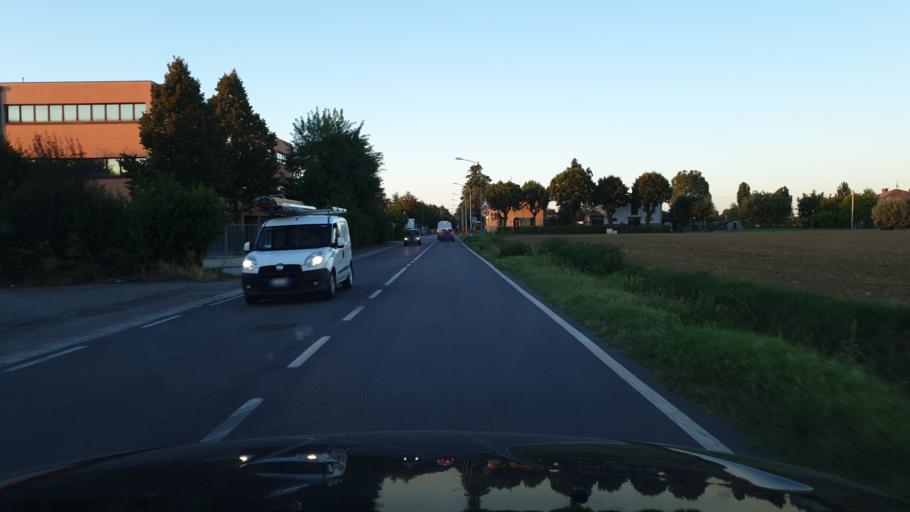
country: IT
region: Emilia-Romagna
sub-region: Provincia di Bologna
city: Quarto Inferiore
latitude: 44.5447
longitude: 11.3964
